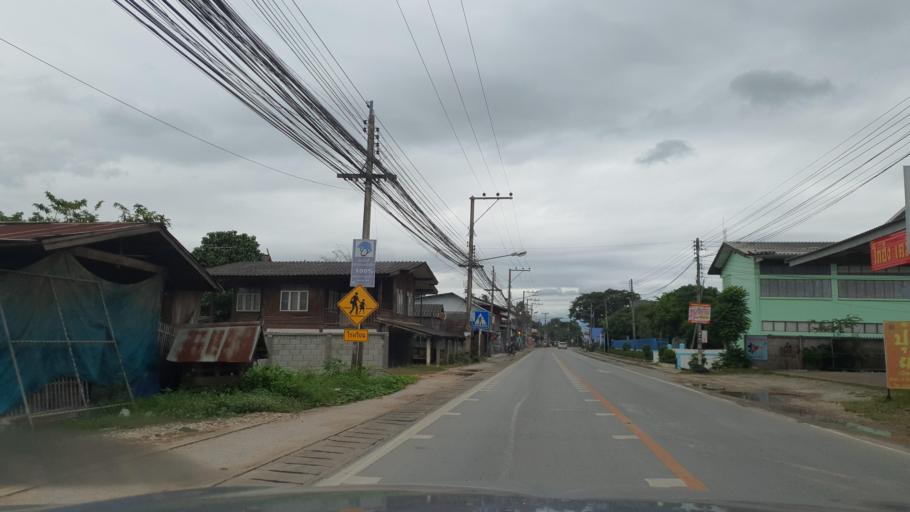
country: TH
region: Chiang Mai
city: San Pa Tong
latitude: 18.6167
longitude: 98.9504
